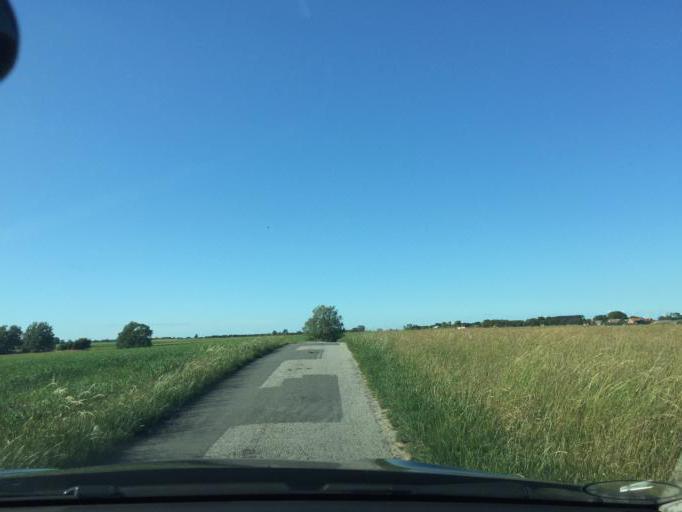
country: DK
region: Zealand
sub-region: Slagelse Kommune
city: Skaelskor
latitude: 55.2049
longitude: 11.1819
